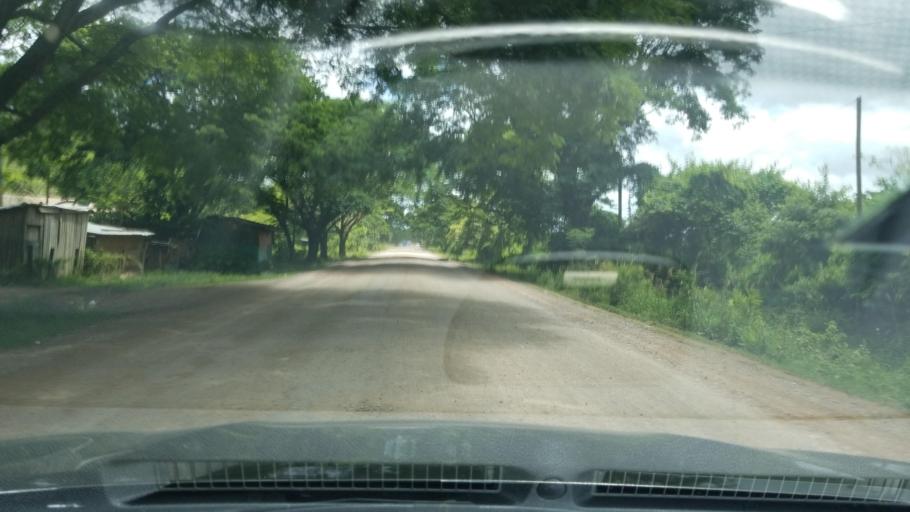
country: HN
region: Francisco Morazan
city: Talanga
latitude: 14.3906
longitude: -87.0757
